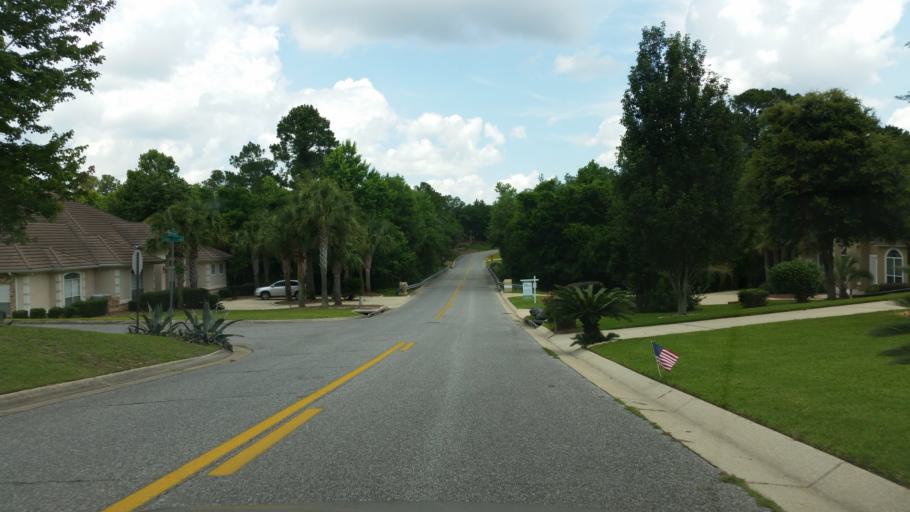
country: US
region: Florida
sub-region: Escambia County
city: Bellview
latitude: 30.4785
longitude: -87.2848
